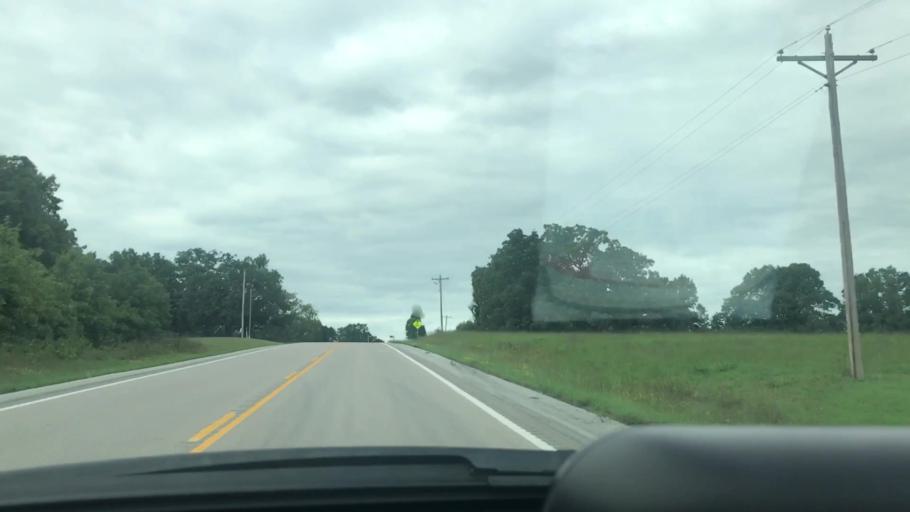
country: US
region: Missouri
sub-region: Benton County
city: Warsaw
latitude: 38.1525
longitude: -93.2951
